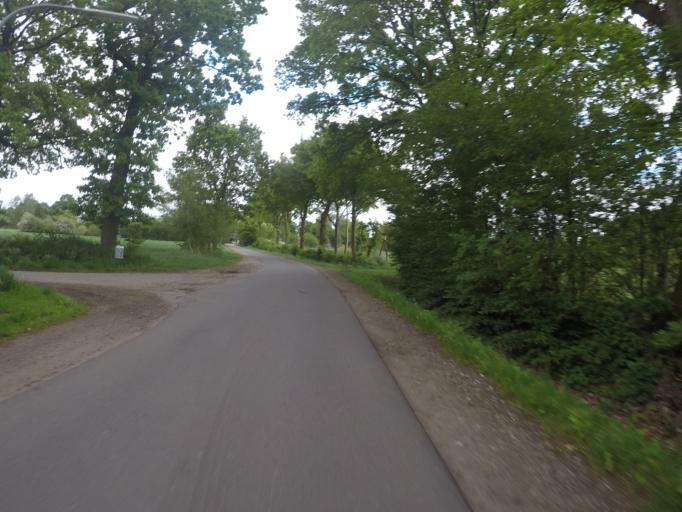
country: DE
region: Schleswig-Holstein
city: Hasloh
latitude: 53.7009
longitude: 9.9217
